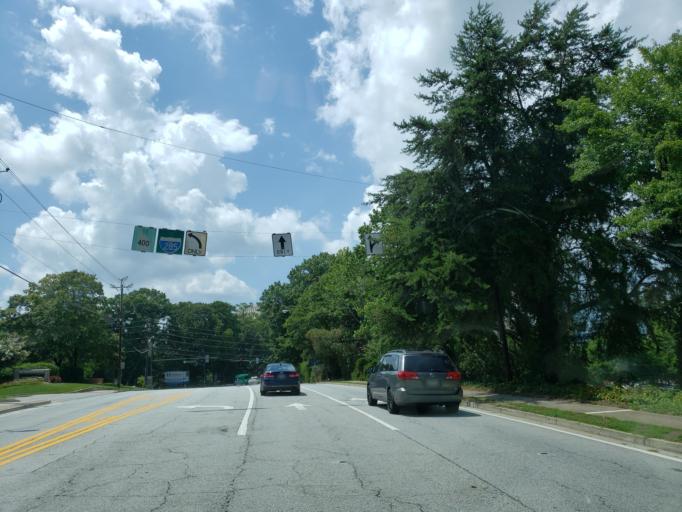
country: US
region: Georgia
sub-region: Fulton County
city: Sandy Springs
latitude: 33.9069
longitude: -84.3514
